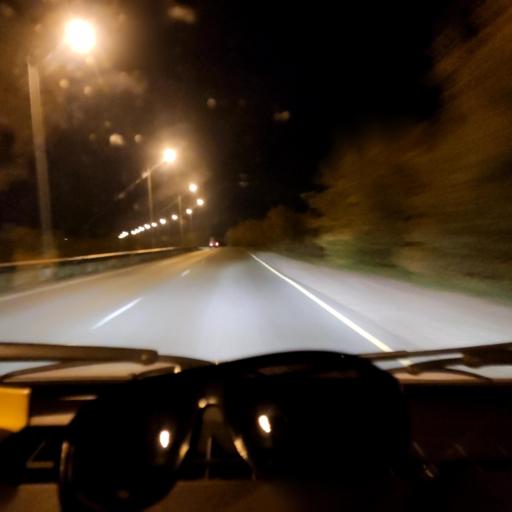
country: RU
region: Bashkortostan
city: Avdon
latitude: 54.5703
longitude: 55.8791
